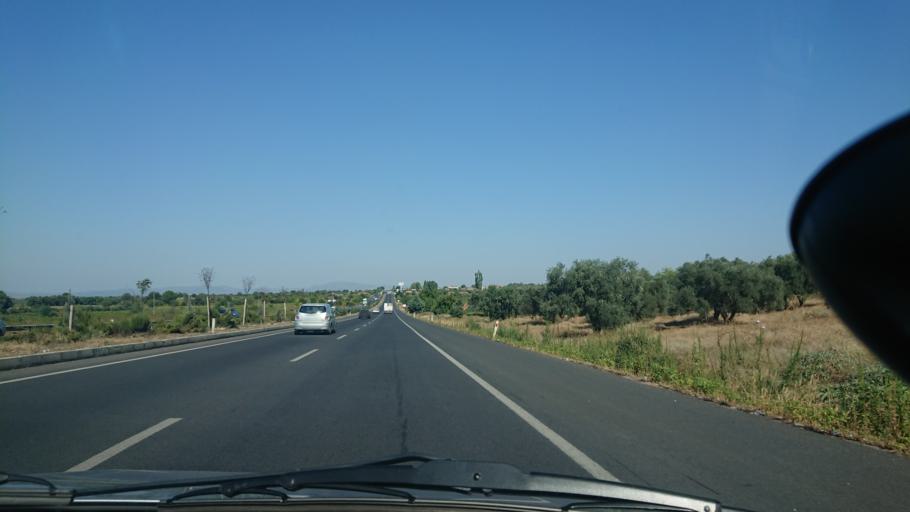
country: TR
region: Manisa
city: Ahmetli
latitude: 38.4935
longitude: 27.8520
